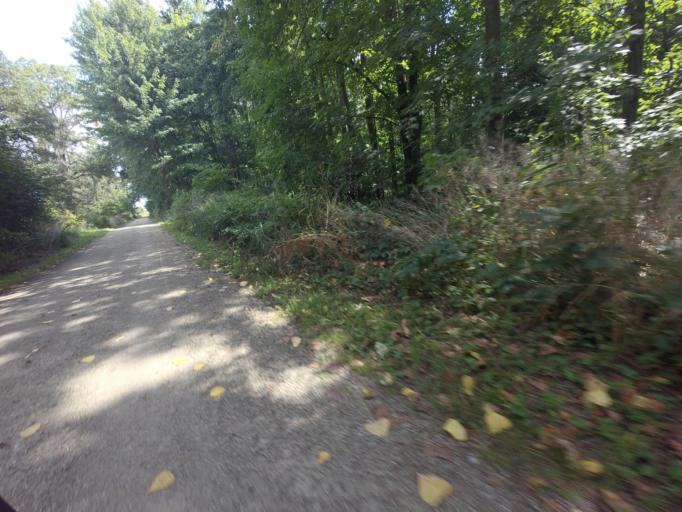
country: CA
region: Ontario
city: North Perth
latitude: 43.5729
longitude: -80.8513
